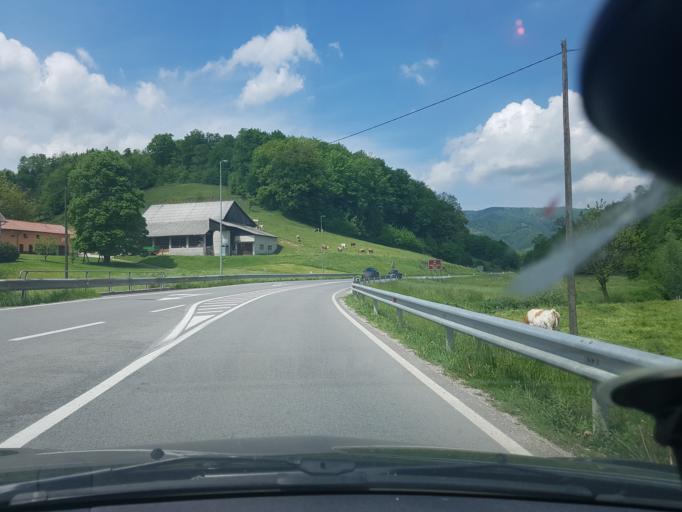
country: SI
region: Rogatec
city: Rogatec
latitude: 46.2283
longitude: 15.6757
